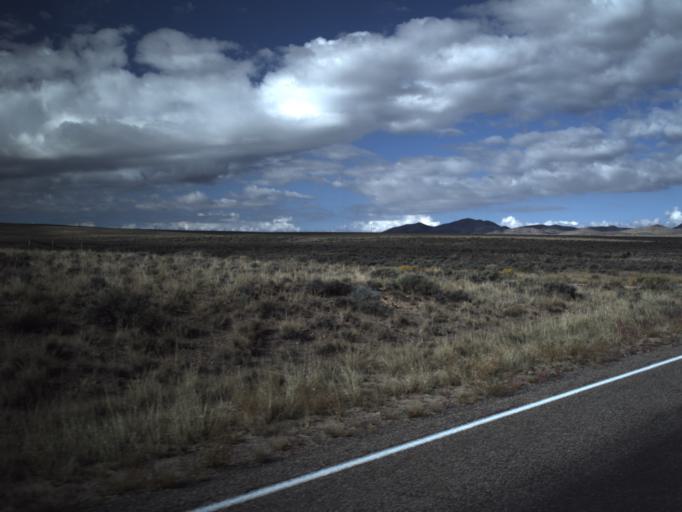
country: US
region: Utah
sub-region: Beaver County
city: Milford
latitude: 38.4353
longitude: -113.1390
